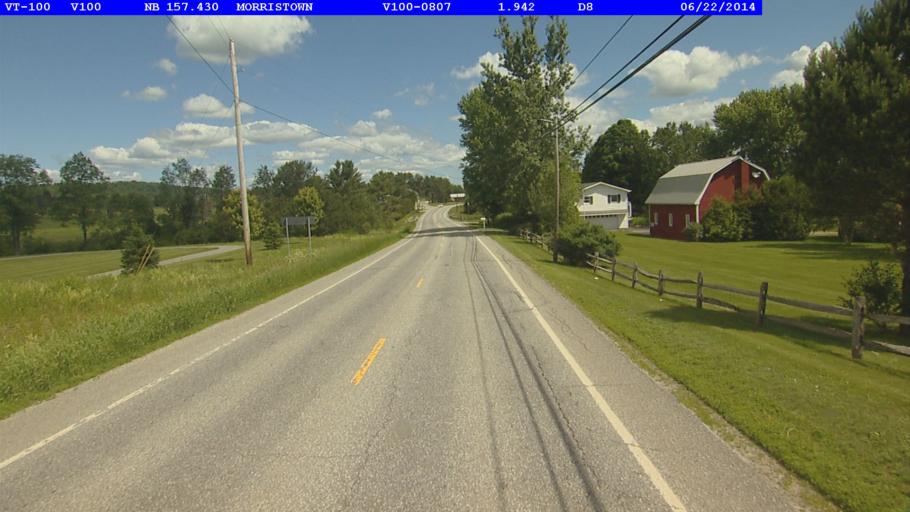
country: US
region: Vermont
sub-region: Lamoille County
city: Morristown
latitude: 44.5203
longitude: -72.6199
